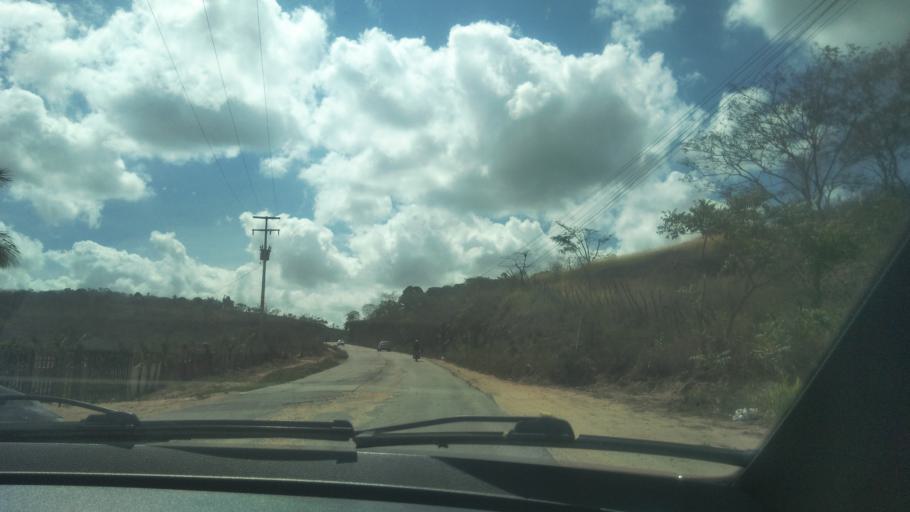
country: BR
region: Pernambuco
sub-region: Vitoria De Santo Antao
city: Vitoria de Santo Antao
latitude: -8.1332
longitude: -35.2806
